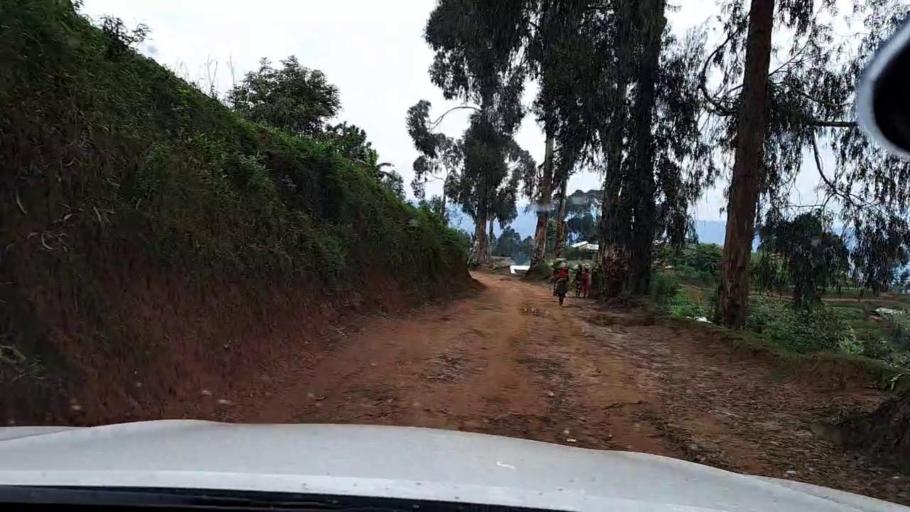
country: RW
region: Southern Province
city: Nzega
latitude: -2.3799
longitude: 29.2425
